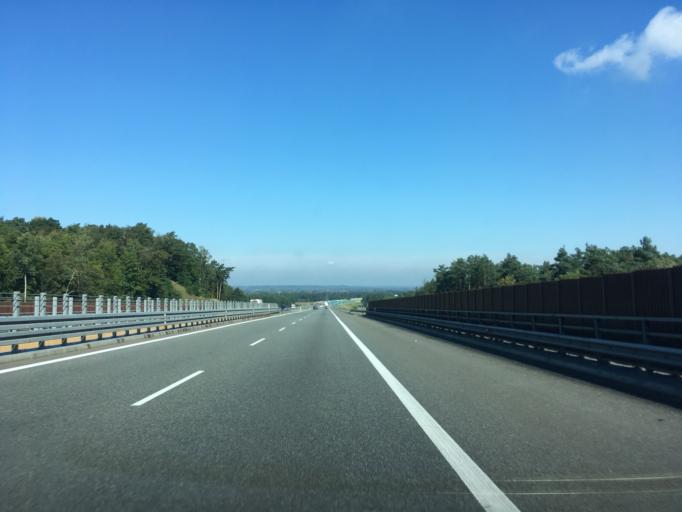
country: PL
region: Kujawsko-Pomorskie
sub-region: Powiat chelminski
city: Lisewo
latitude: 53.3910
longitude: 18.6859
